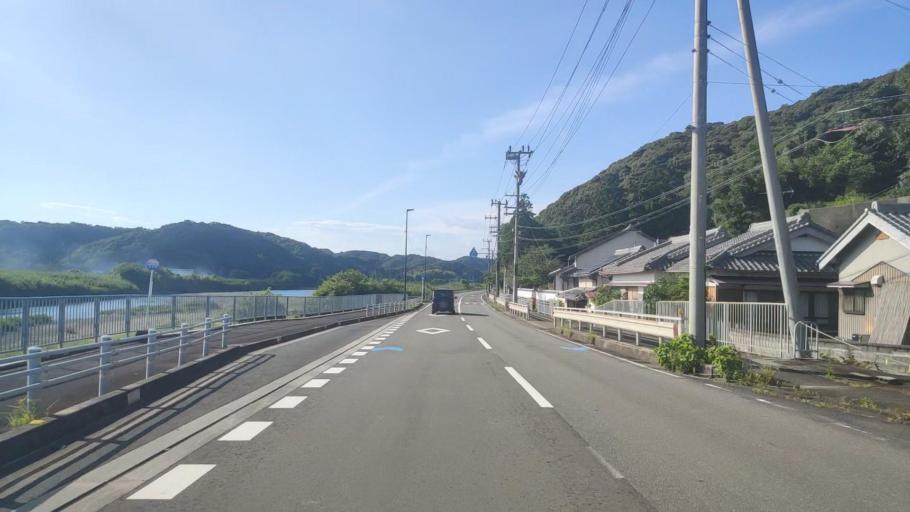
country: JP
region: Wakayama
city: Tanabe
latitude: 33.6540
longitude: 135.4025
